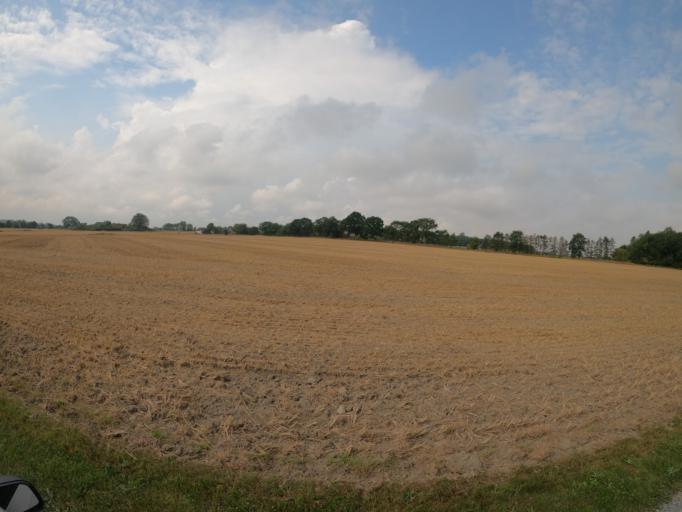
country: SE
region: Skane
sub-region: Lunds Kommun
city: Lund
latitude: 55.7234
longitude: 13.2932
